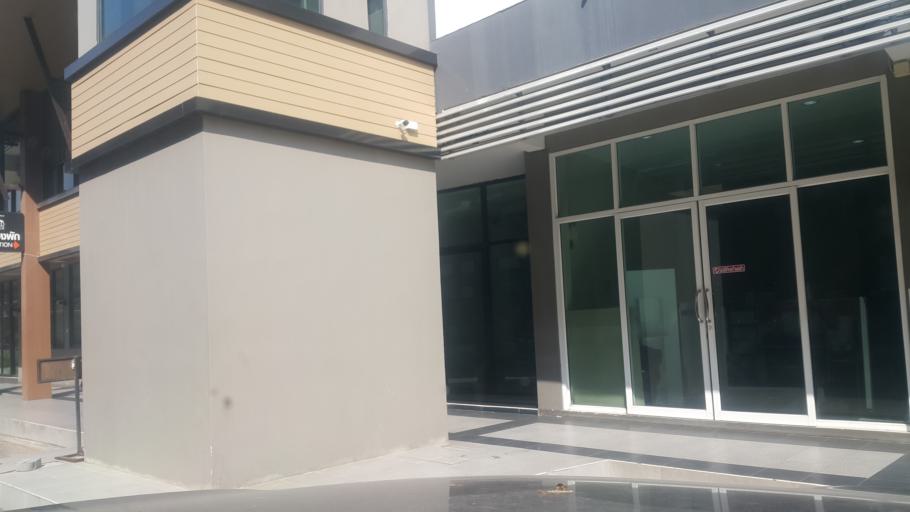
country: TH
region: Nakhon Ratchasima
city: Nakhon Ratchasima
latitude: 14.9521
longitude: 102.0453
